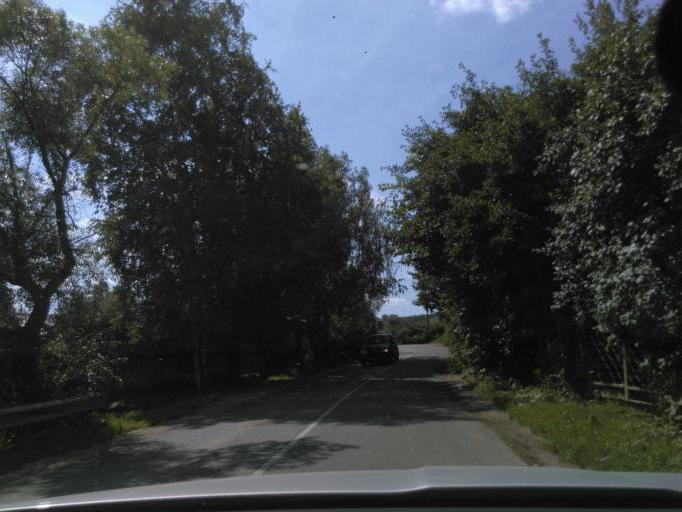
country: RU
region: Moskovskaya
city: Solnechnogorsk
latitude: 56.1642
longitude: 36.9764
